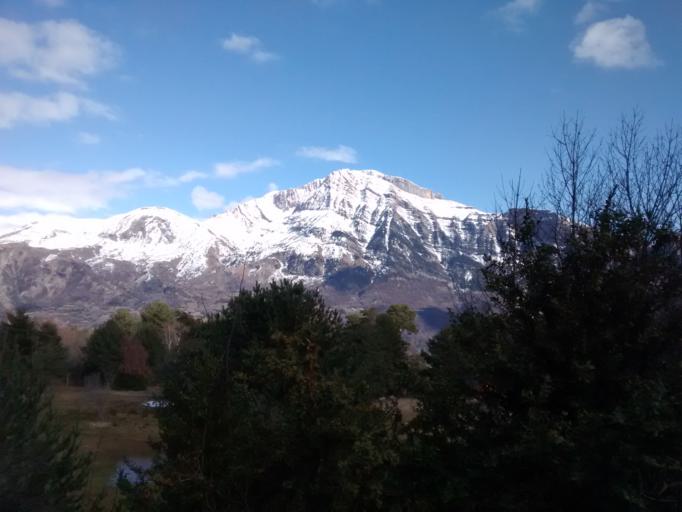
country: ES
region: Aragon
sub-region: Provincia de Huesca
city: Hoz de Jaca
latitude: 42.6966
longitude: -0.3381
